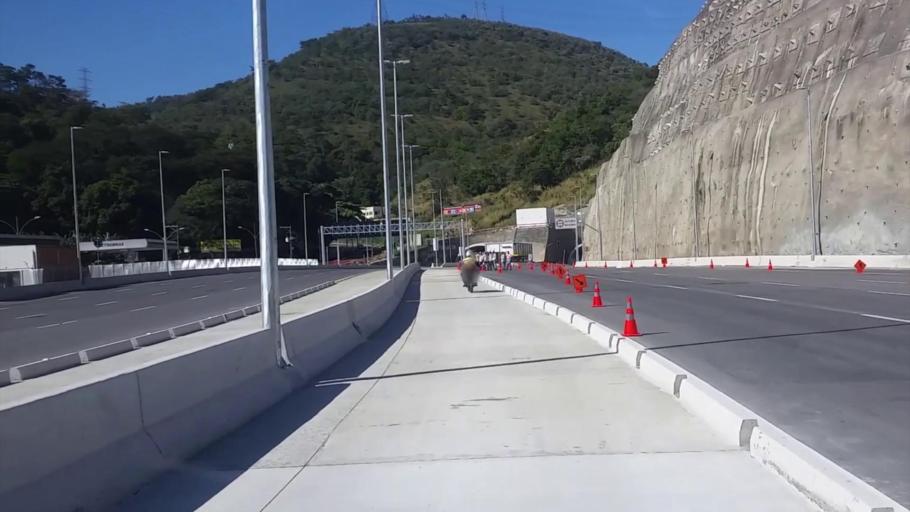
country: BR
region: Rio de Janeiro
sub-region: Nilopolis
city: Nilopolis
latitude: -22.8879
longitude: -43.4010
